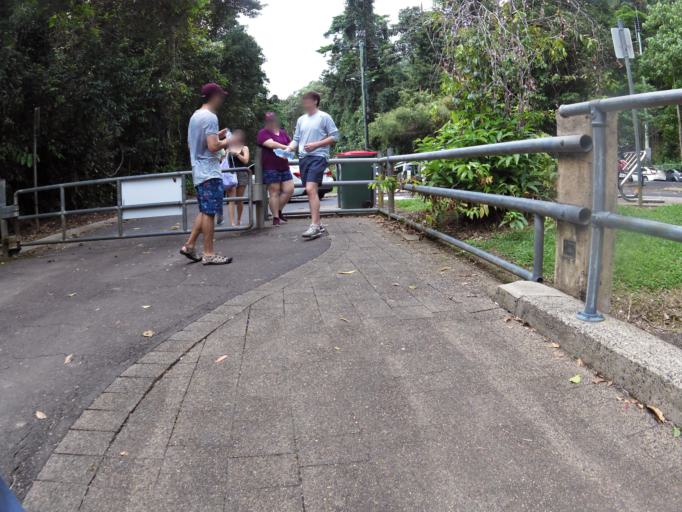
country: AU
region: Queensland
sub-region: Cairns
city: Woree
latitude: -16.9622
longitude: 145.6795
